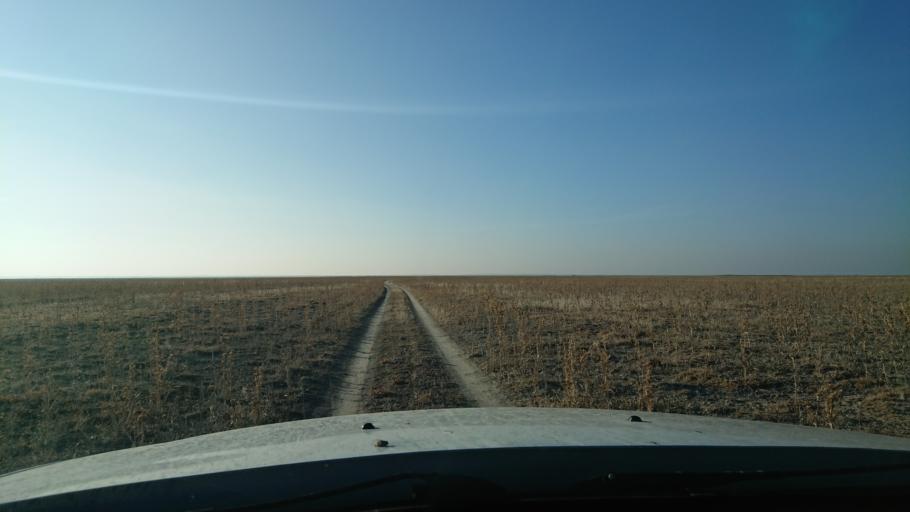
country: TR
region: Aksaray
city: Sultanhani
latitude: 38.3717
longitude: 33.5479
